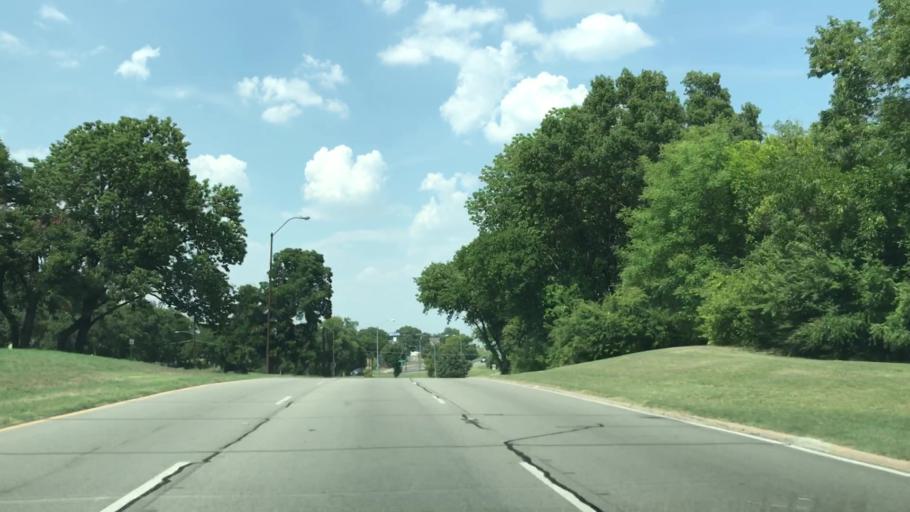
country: US
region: Texas
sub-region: Dallas County
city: Highland Park
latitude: 32.8032
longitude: -96.7358
